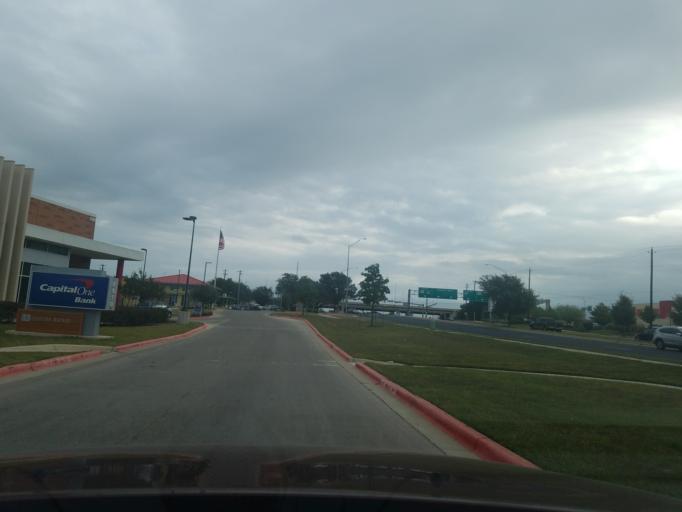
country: US
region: Texas
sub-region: Williamson County
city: Anderson Mill
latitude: 30.4785
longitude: -97.8054
